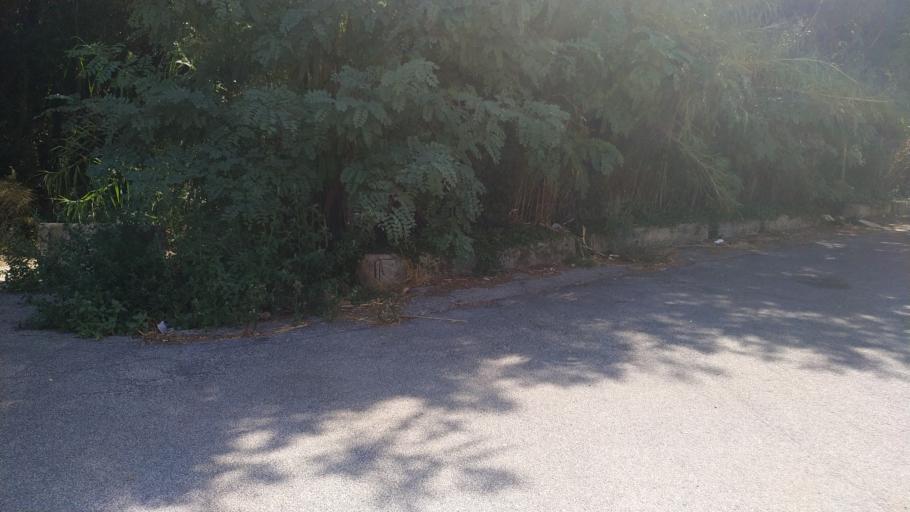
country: IT
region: Latium
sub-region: Citta metropolitana di Roma Capitale
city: Lido di Ostia
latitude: 41.7310
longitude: 12.3053
